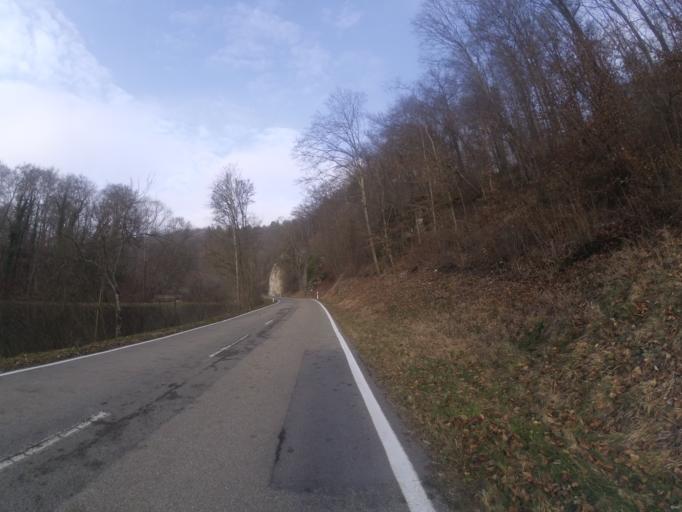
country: DE
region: Baden-Wuerttemberg
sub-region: Tuebingen Region
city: Lauterach
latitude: 48.2592
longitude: 9.5747
